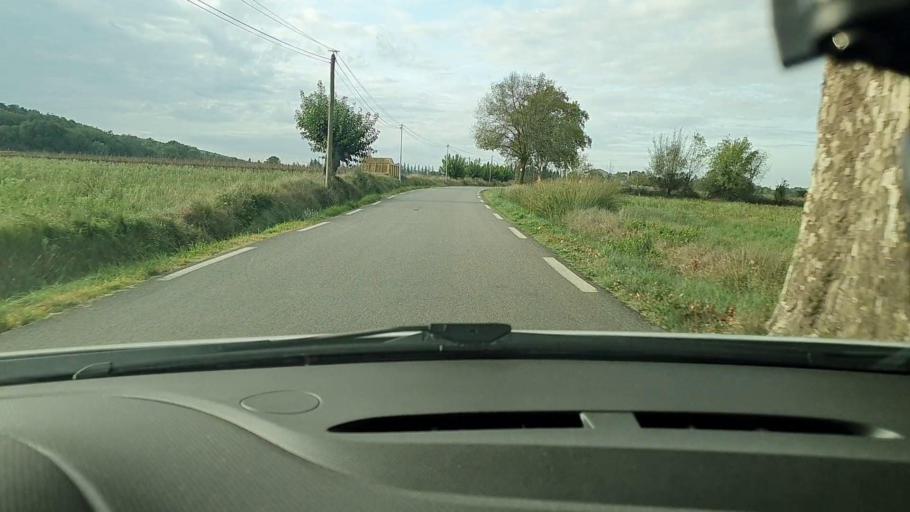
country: FR
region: Languedoc-Roussillon
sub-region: Departement du Gard
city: Les Mages
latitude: 44.1902
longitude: 4.2375
